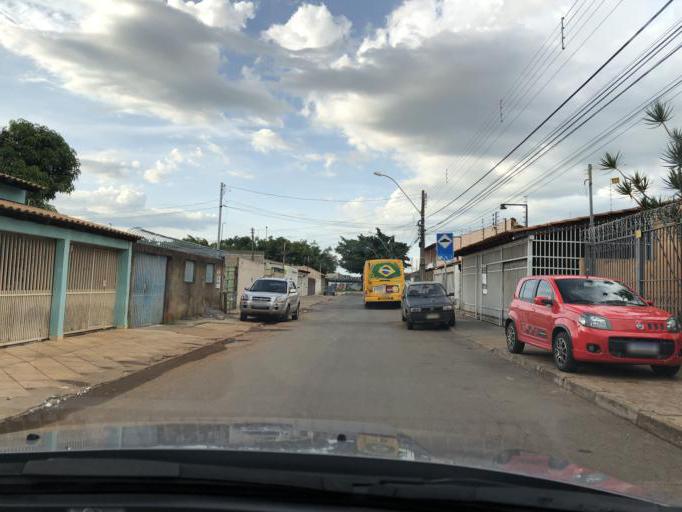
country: BR
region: Federal District
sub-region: Brasilia
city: Brasilia
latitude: -15.8169
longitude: -48.1070
